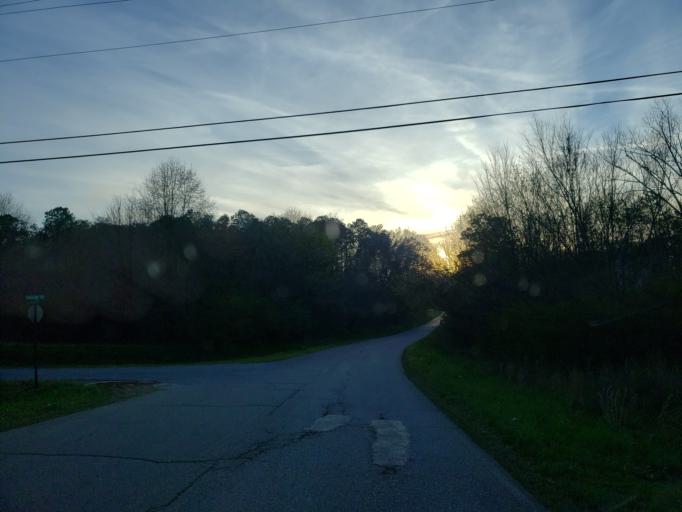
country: US
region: Georgia
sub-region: Polk County
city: Rockmart
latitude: 33.9957
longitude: -85.0290
